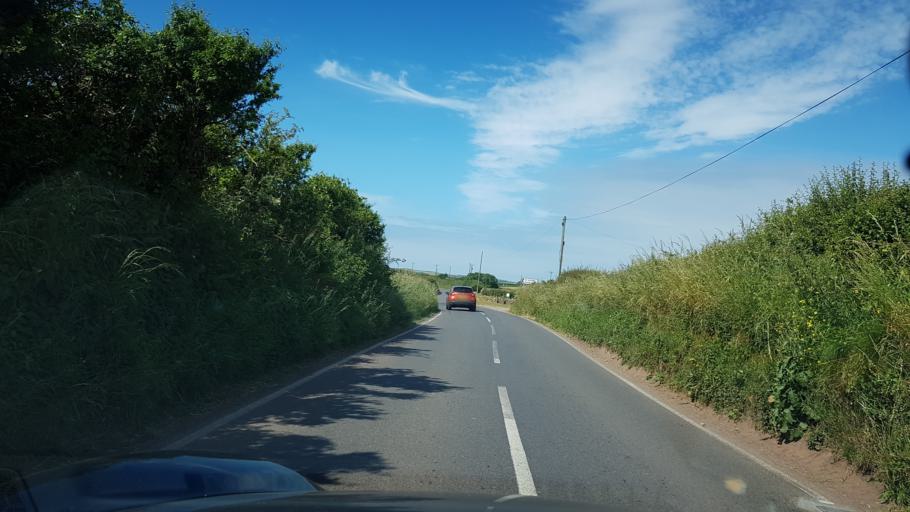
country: GB
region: Wales
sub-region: Pembrokeshire
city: Herbrandston
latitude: 51.7522
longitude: -5.1261
